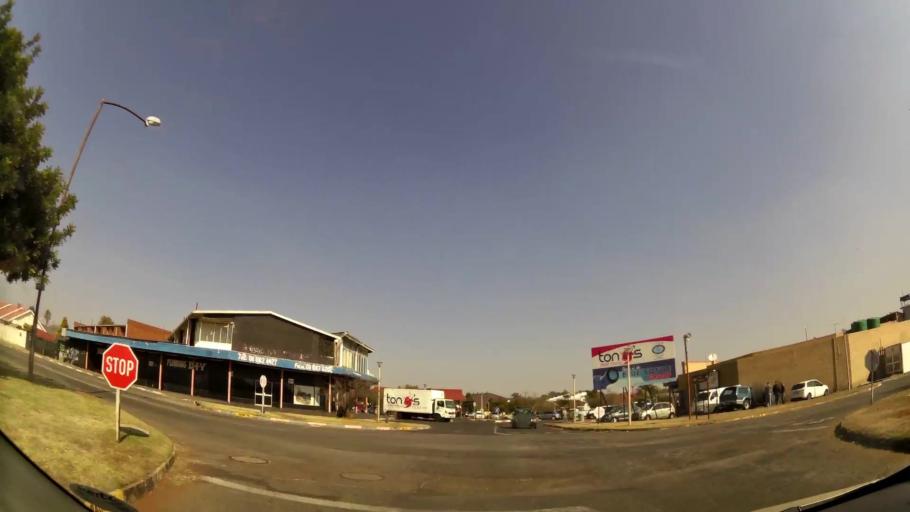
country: ZA
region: Gauteng
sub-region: West Rand District Municipality
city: Randfontein
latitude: -26.1654
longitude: 27.6987
